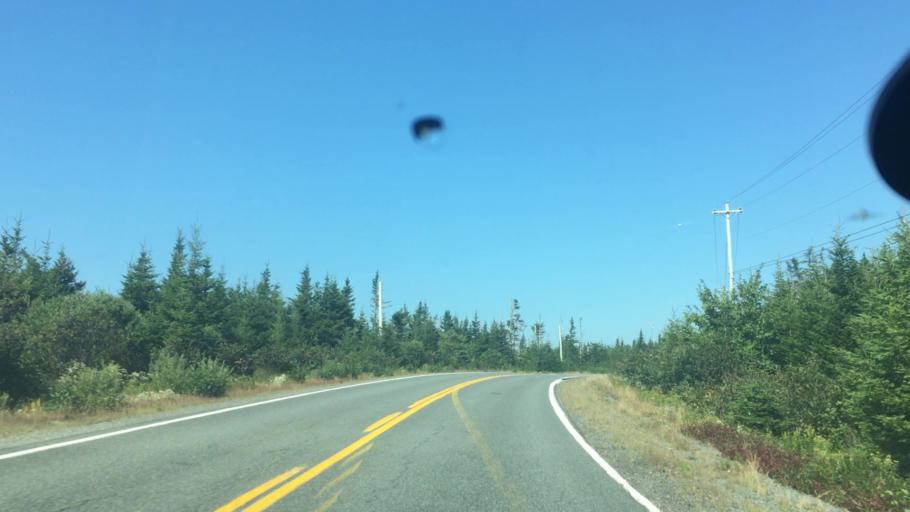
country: CA
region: Nova Scotia
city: Antigonish
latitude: 44.9838
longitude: -62.0956
